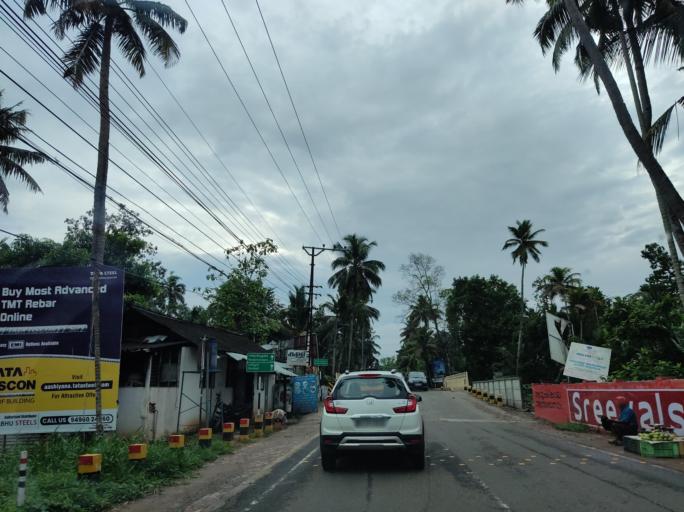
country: IN
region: Kerala
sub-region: Alappuzha
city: Mavelikara
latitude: 9.2516
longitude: 76.5014
